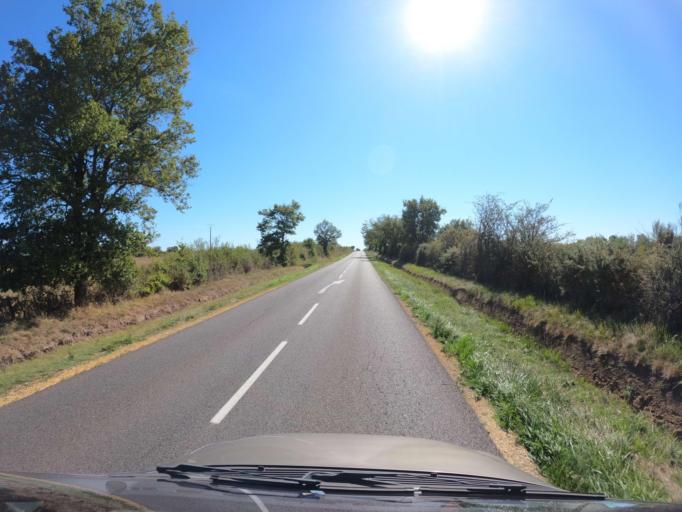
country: FR
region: Poitou-Charentes
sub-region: Departement de la Vienne
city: Saulge
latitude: 46.3841
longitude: 0.9164
